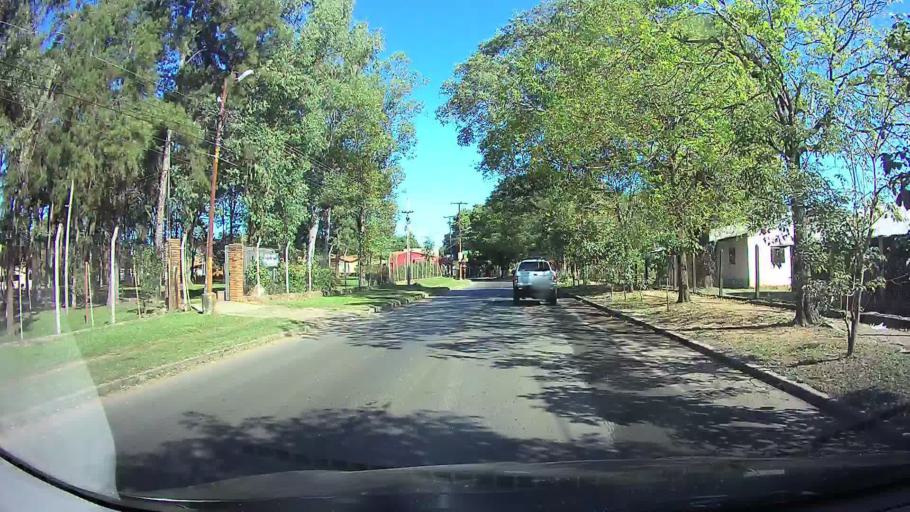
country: PY
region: Central
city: Fernando de la Mora
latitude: -25.3431
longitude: -57.5199
